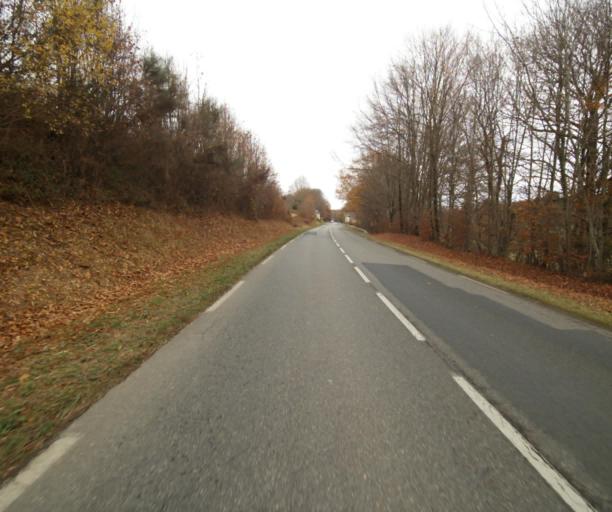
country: FR
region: Limousin
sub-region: Departement de la Correze
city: Sainte-Fortunade
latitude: 45.1883
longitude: 1.7663
